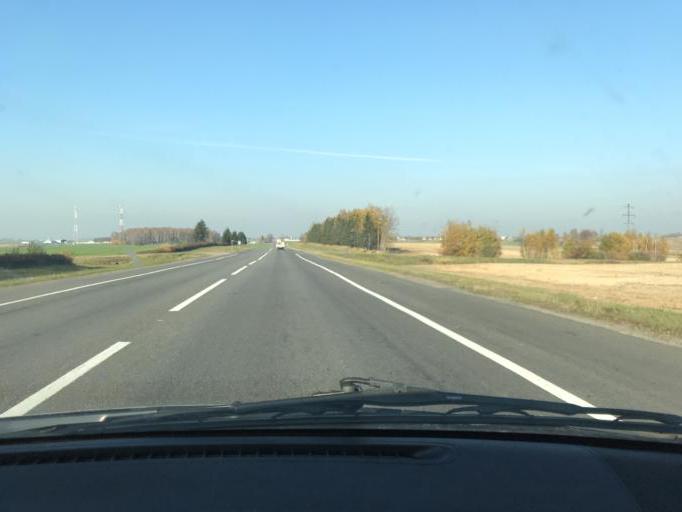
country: BY
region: Mogilev
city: Shklow
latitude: 54.2237
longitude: 30.4522
